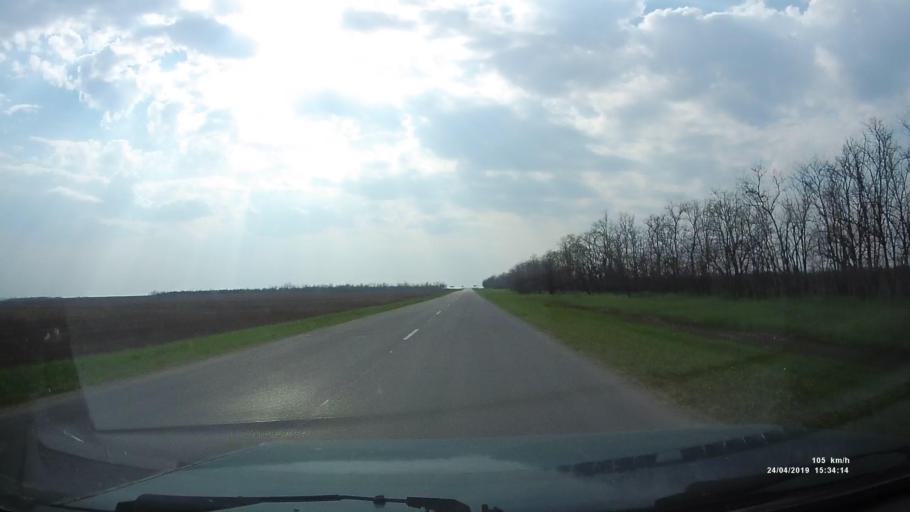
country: RU
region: Kalmykiya
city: Yashalta
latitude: 46.5993
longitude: 42.9206
